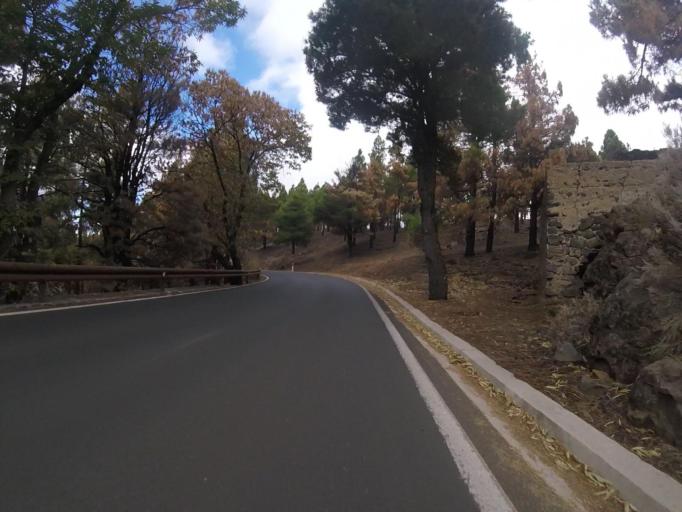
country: ES
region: Canary Islands
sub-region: Provincia de Las Palmas
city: Tejeda
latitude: 27.9734
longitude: -15.5758
